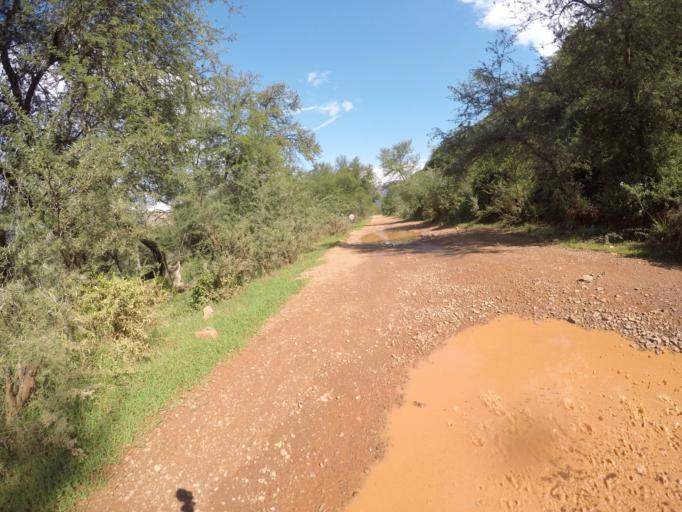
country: ZA
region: Eastern Cape
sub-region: Cacadu District Municipality
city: Kareedouw
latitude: -33.6606
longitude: 24.3962
